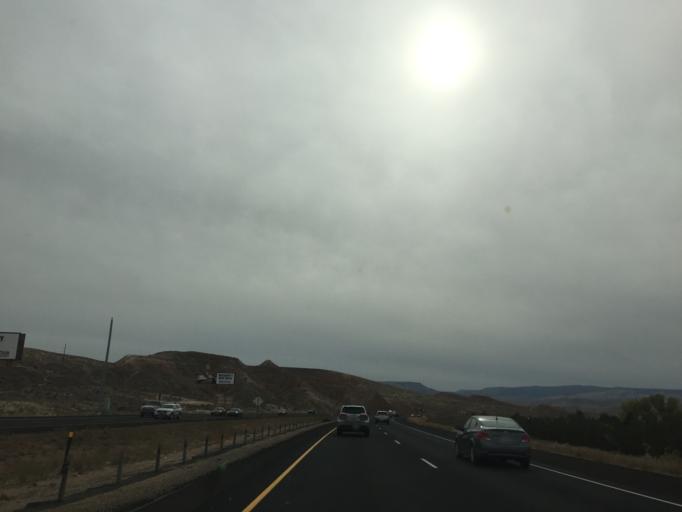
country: US
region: Utah
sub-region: Washington County
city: Saint George
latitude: 37.0515
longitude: -113.5884
